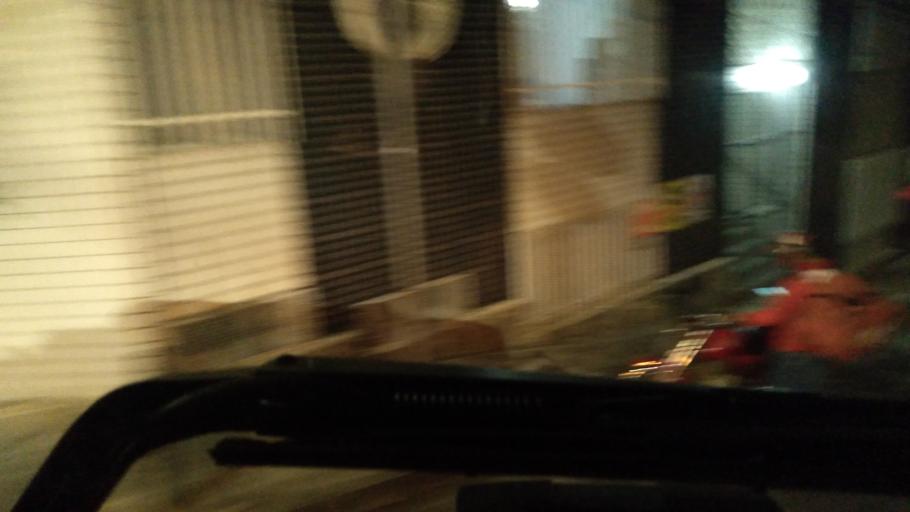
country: BR
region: Minas Gerais
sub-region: Belo Horizonte
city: Belo Horizonte
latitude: -19.9199
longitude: -43.9809
